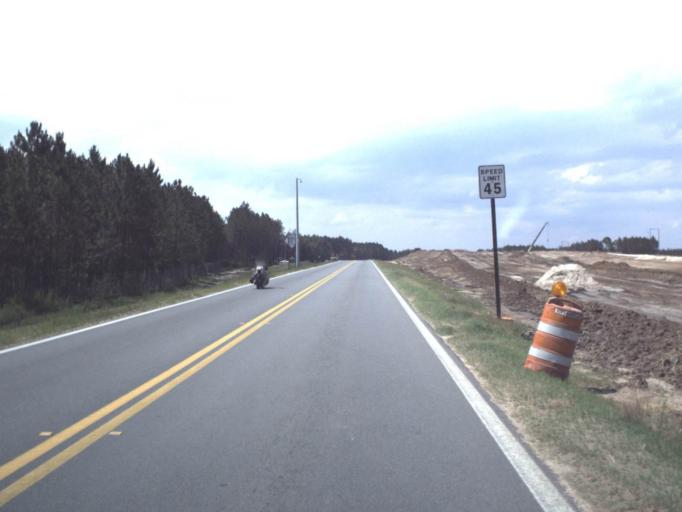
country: US
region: Florida
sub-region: Clay County
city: Lakeside
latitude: 30.1903
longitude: -81.8377
